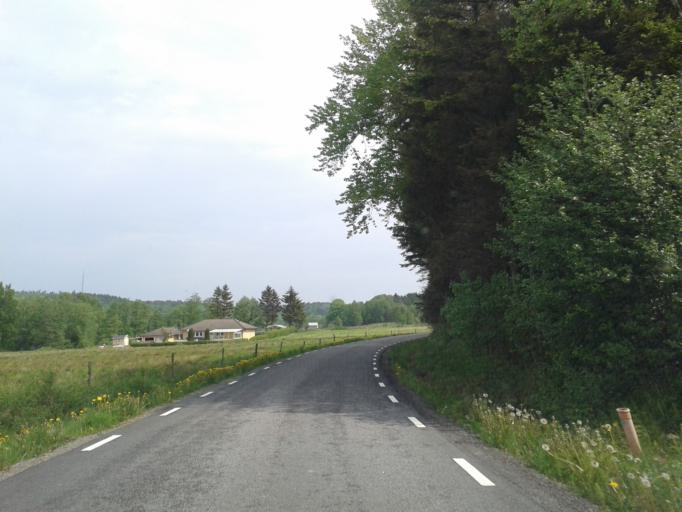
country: SE
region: Vaestra Goetaland
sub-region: Kungalvs Kommun
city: Kungalv
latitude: 57.9221
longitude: 11.9610
